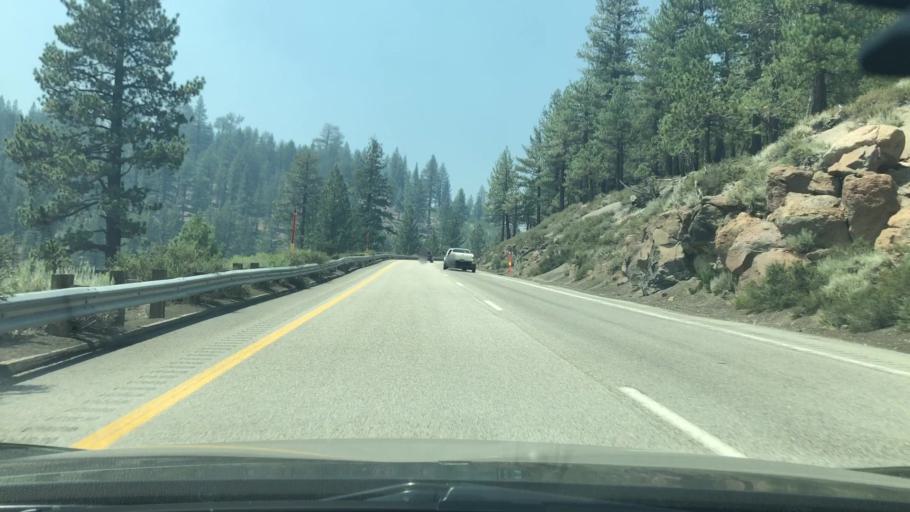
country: US
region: California
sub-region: Mono County
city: Mammoth Lakes
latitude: 37.7596
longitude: -118.9906
